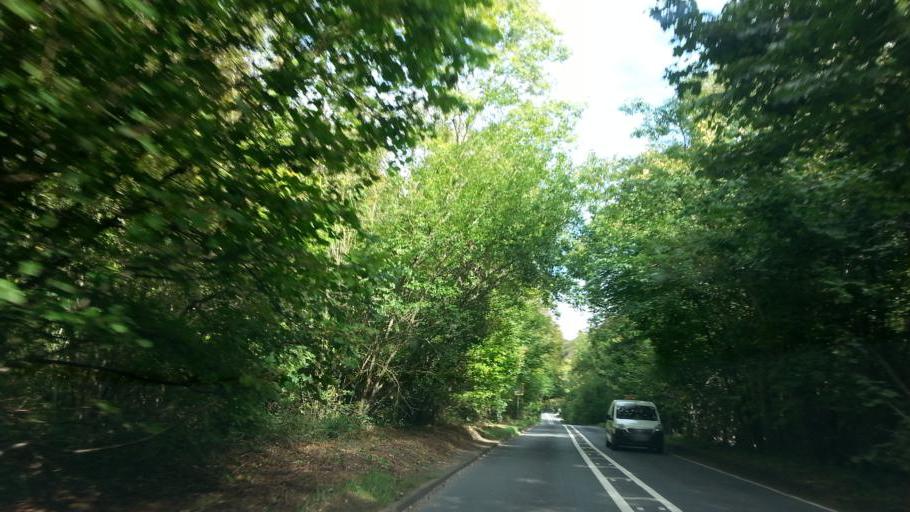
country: GB
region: England
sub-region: Gloucestershire
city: Painswick
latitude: 51.8136
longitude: -2.1761
